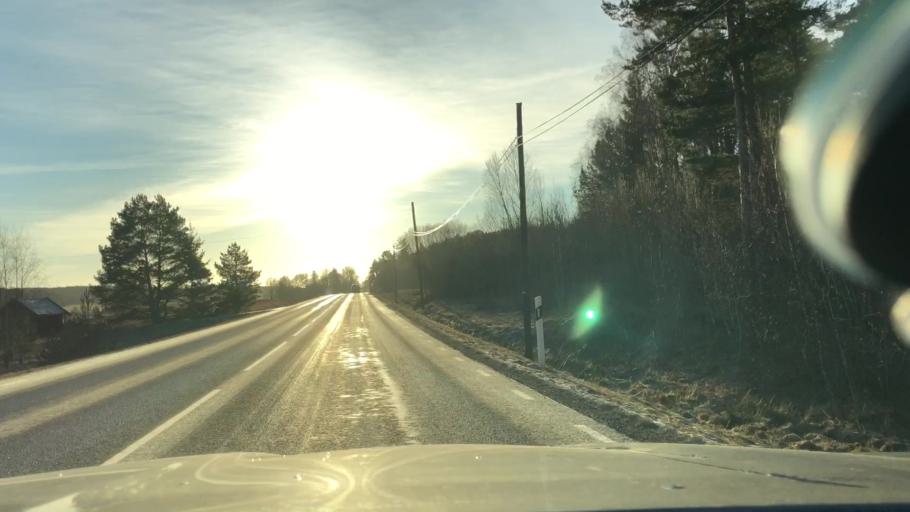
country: SE
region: Stockholm
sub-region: Sodertalje Kommun
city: Pershagen
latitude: 59.0409
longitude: 17.6030
